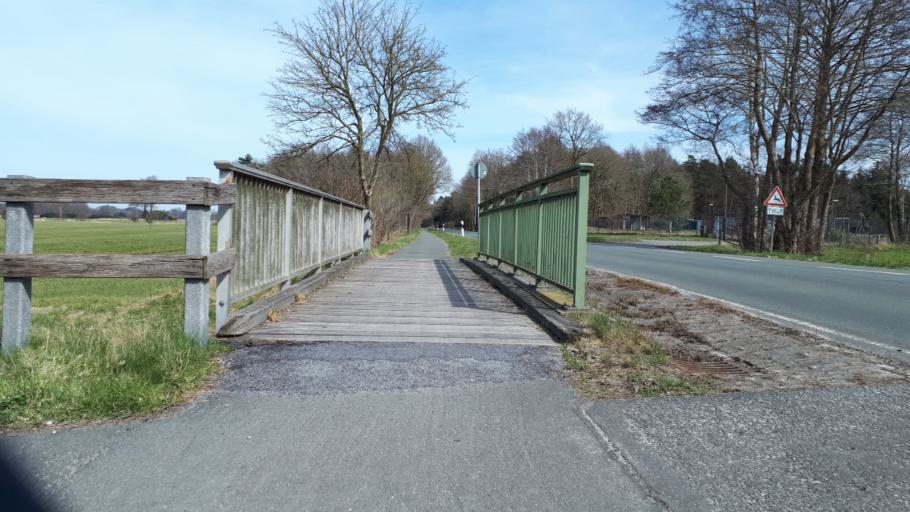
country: DE
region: Lower Saxony
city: Wardenburg
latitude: 53.0403
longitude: 8.1666
